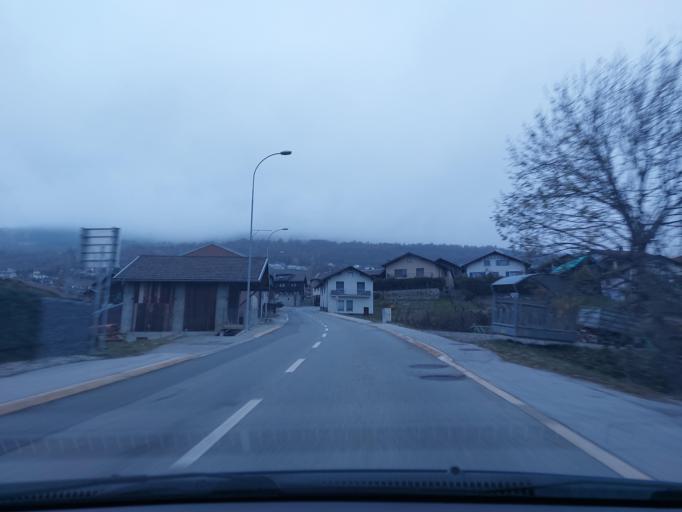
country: CH
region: Valais
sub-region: Sion District
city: Saviese
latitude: 46.2451
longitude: 7.3476
